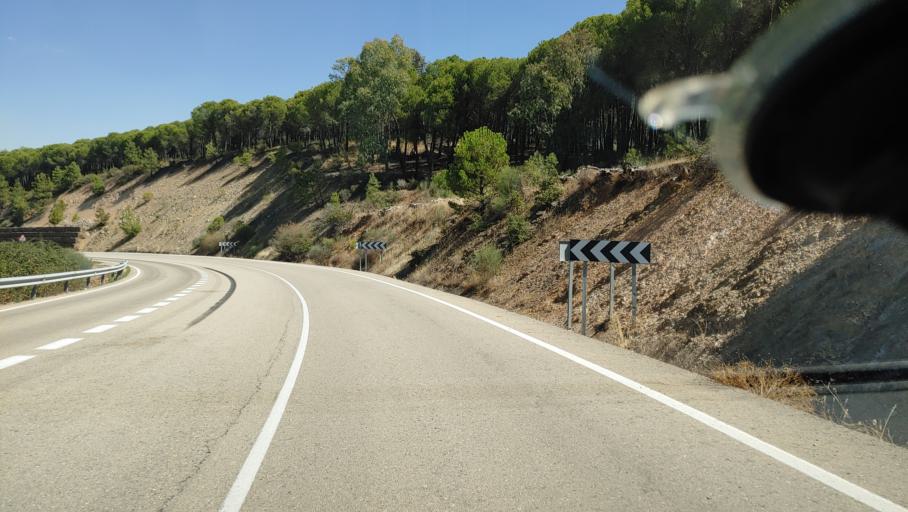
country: ES
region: Castille-La Mancha
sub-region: Provincia de Ciudad Real
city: Saceruela
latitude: 39.0072
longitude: -4.5087
